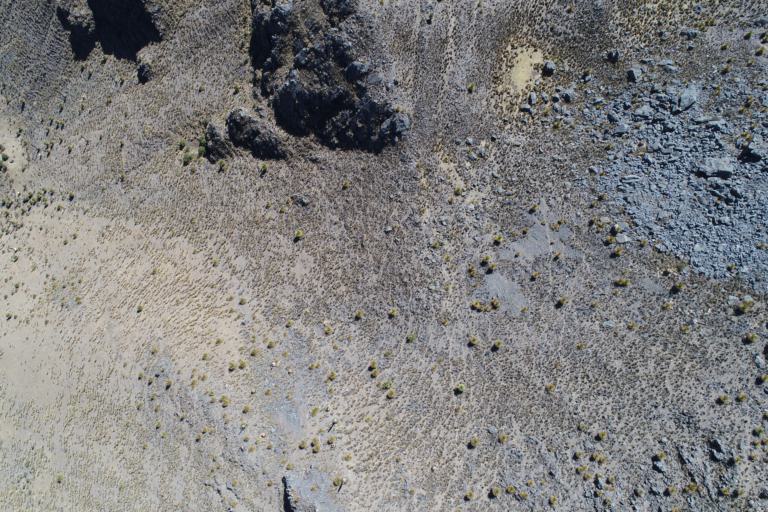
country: BO
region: La Paz
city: Viloco
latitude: -16.8105
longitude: -67.5463
